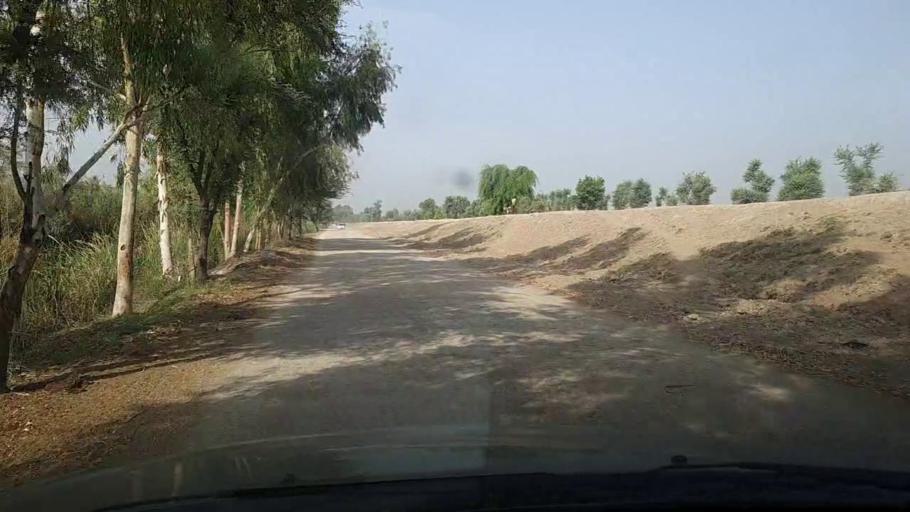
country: PK
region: Sindh
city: Pir jo Goth
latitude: 27.5308
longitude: 68.5031
